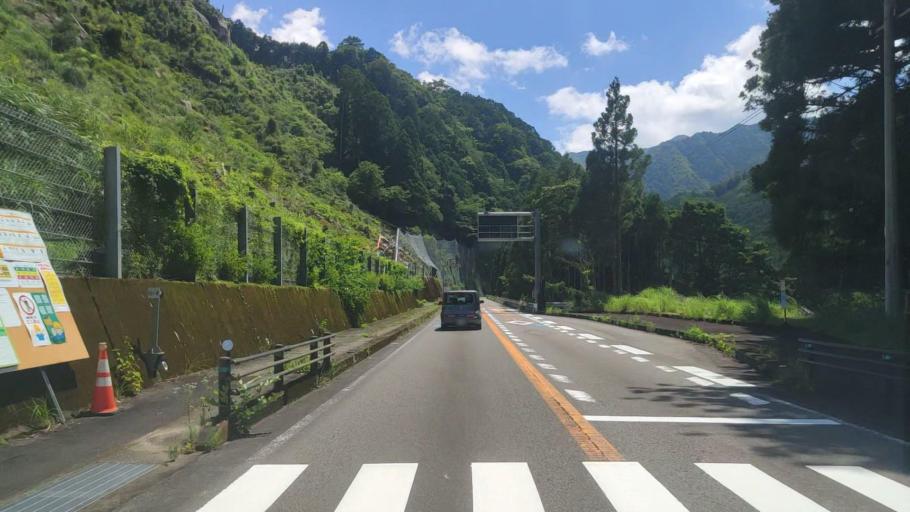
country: JP
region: Mie
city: Owase
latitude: 33.9826
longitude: 136.1077
